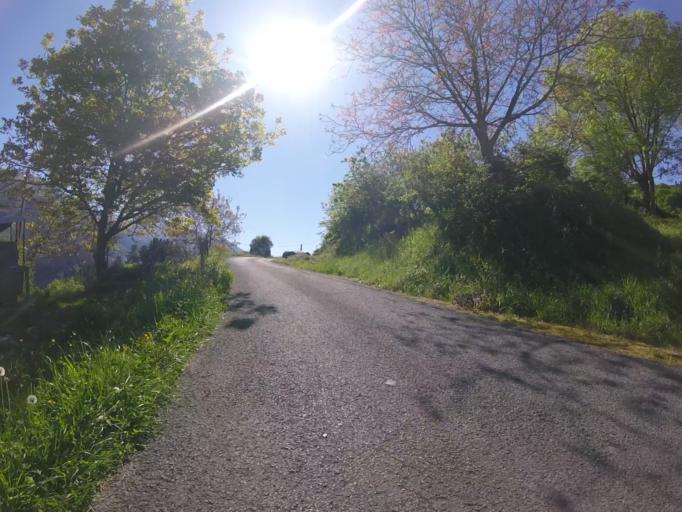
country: ES
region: Basque Country
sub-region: Provincia de Guipuzcoa
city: Errezil
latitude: 43.1702
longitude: -2.2091
